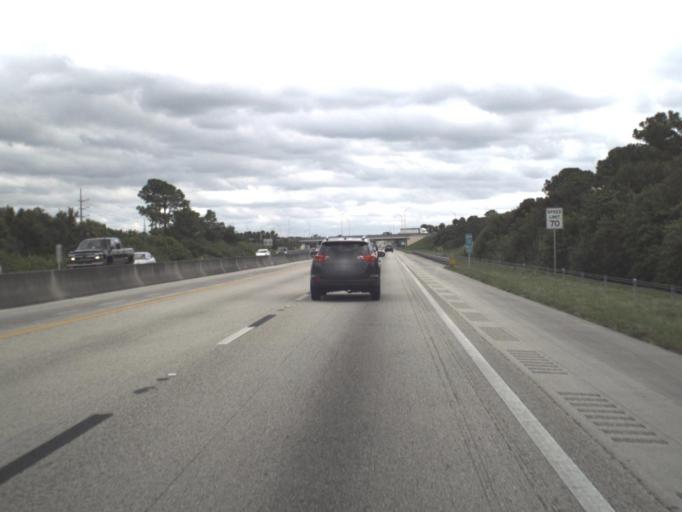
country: US
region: Florida
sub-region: Martin County
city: Palm City
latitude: 27.1298
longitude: -80.2833
